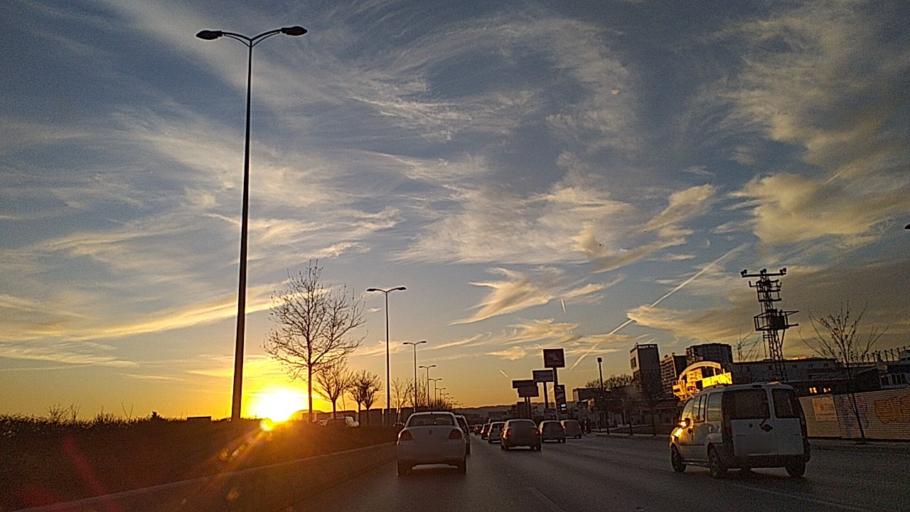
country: TR
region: Ankara
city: Etimesgut
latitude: 39.9638
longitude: 32.6483
